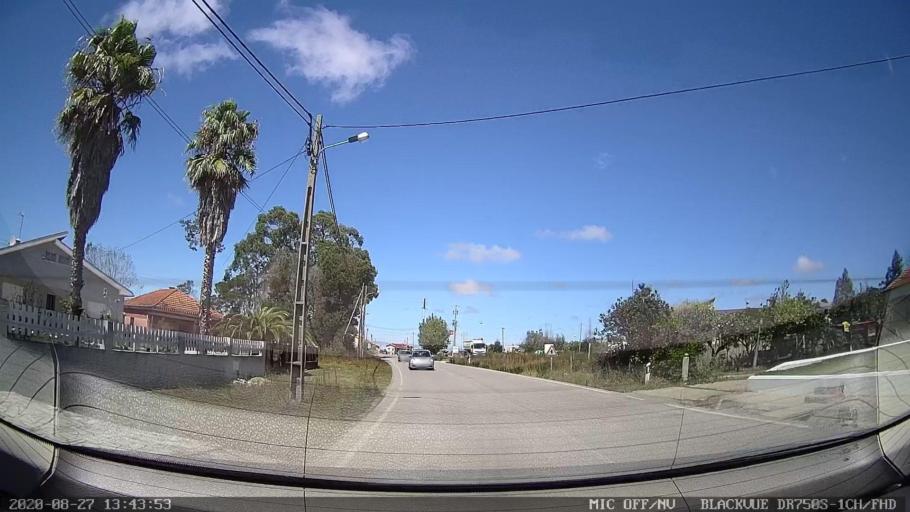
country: PT
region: Coimbra
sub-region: Mira
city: Mira
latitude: 40.4169
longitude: -8.7366
